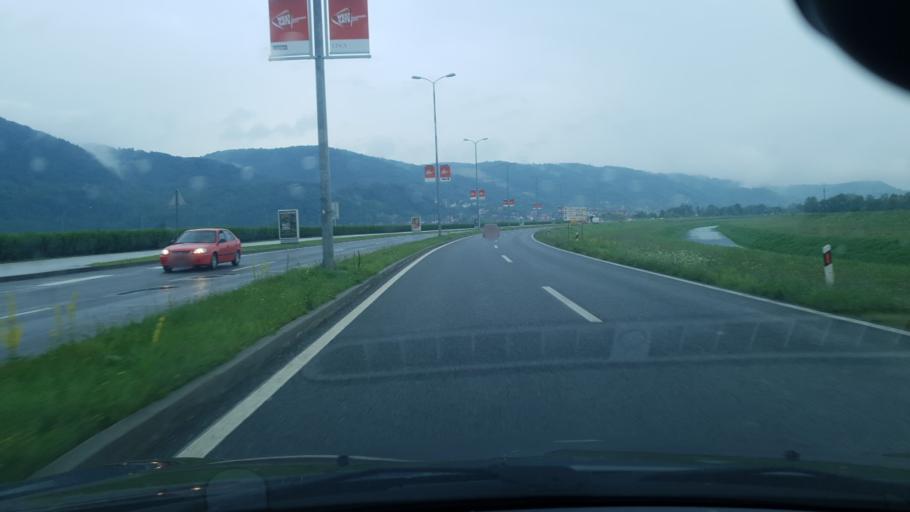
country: HR
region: Zagrebacka
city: Zapresic
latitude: 45.8676
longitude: 15.8260
